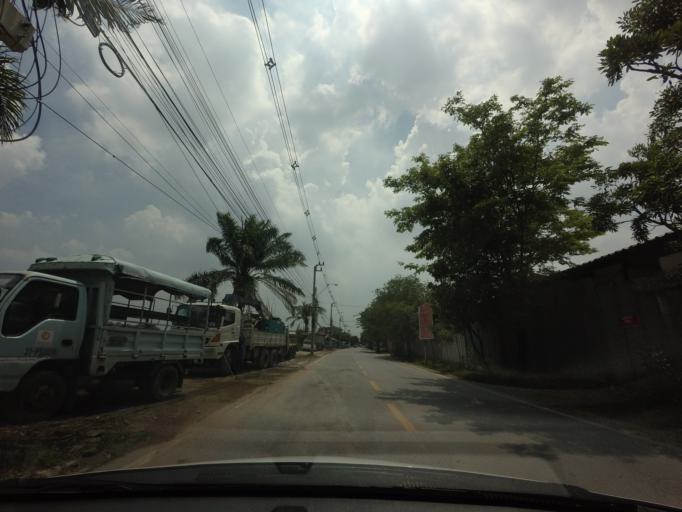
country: TH
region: Bangkok
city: Taling Chan
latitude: 13.7747
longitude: 100.4126
